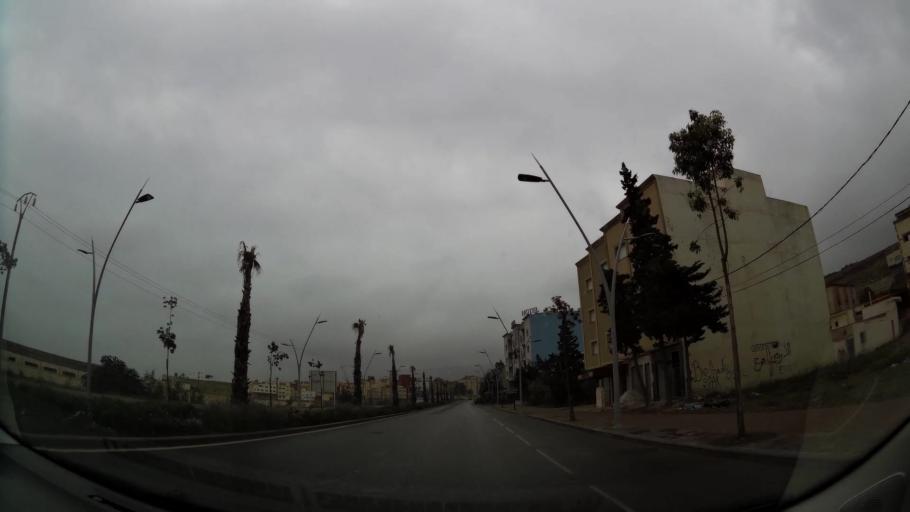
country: MA
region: Oriental
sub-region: Nador
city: Nador
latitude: 35.1936
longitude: -2.9313
